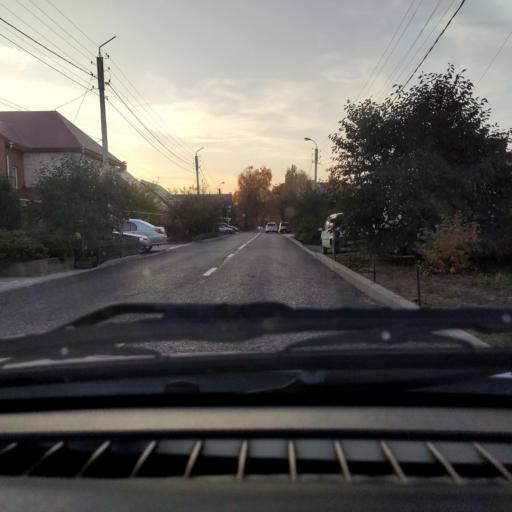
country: RU
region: Samara
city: Tol'yatti
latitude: 53.5295
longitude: 49.4198
